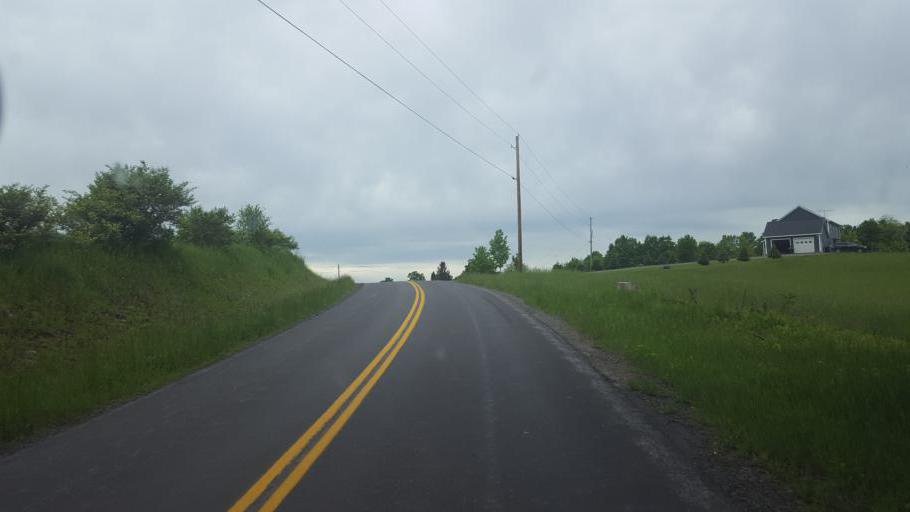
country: US
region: New York
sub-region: Herkimer County
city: Frankfort
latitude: 42.9206
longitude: -75.1378
